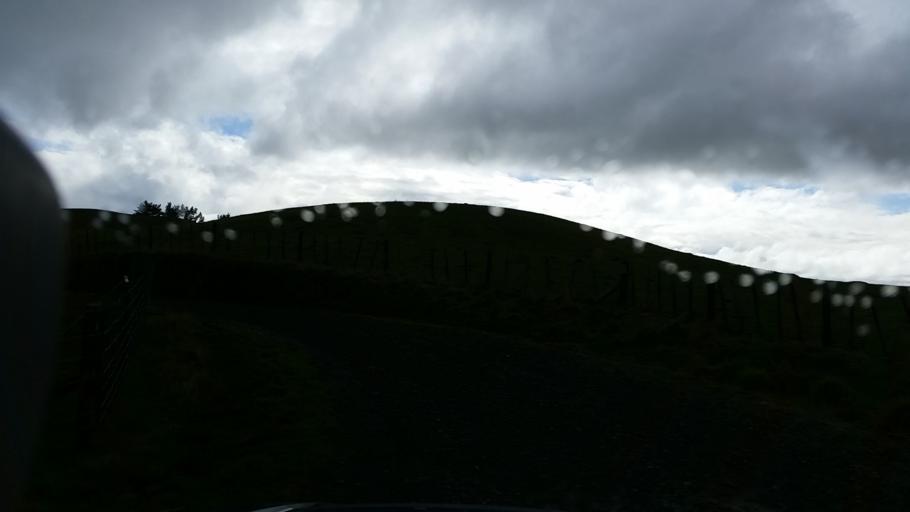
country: NZ
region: Taranaki
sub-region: South Taranaki District
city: Eltham
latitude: -39.2754
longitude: 174.3399
